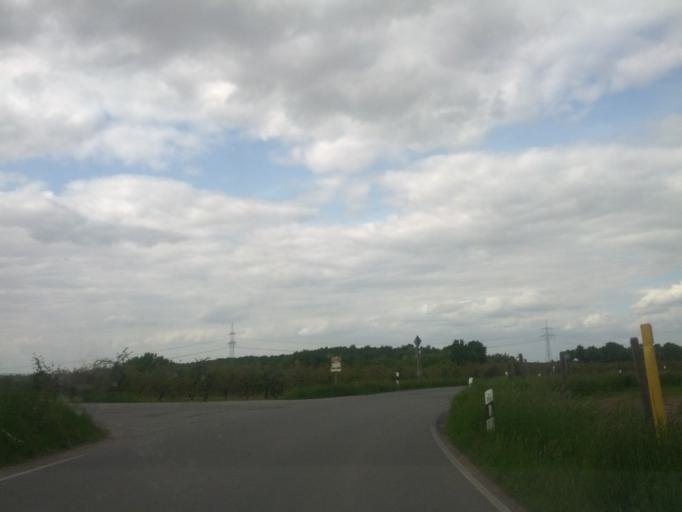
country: DE
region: Saxony
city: Kreischa
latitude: 50.9434
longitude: 13.7925
